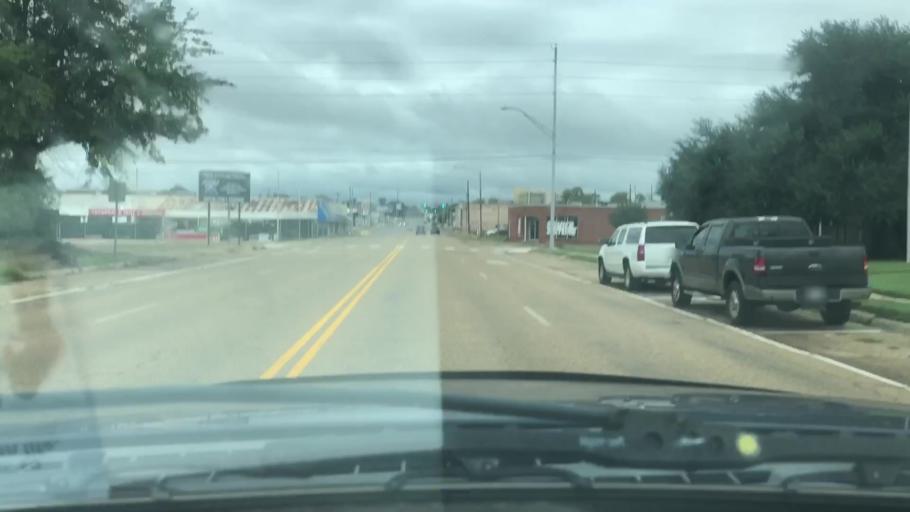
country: US
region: Texas
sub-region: Bowie County
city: Texarkana
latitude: 33.4237
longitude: -94.0471
